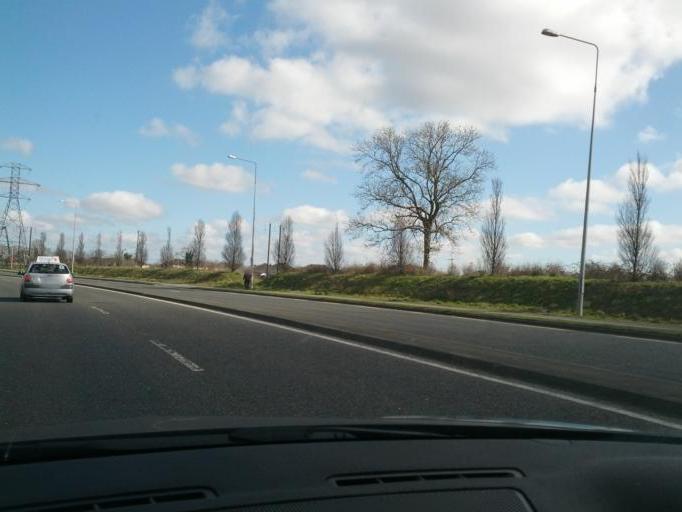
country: IE
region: Leinster
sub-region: Kildare
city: Leixlip
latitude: 53.3675
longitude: -6.5233
